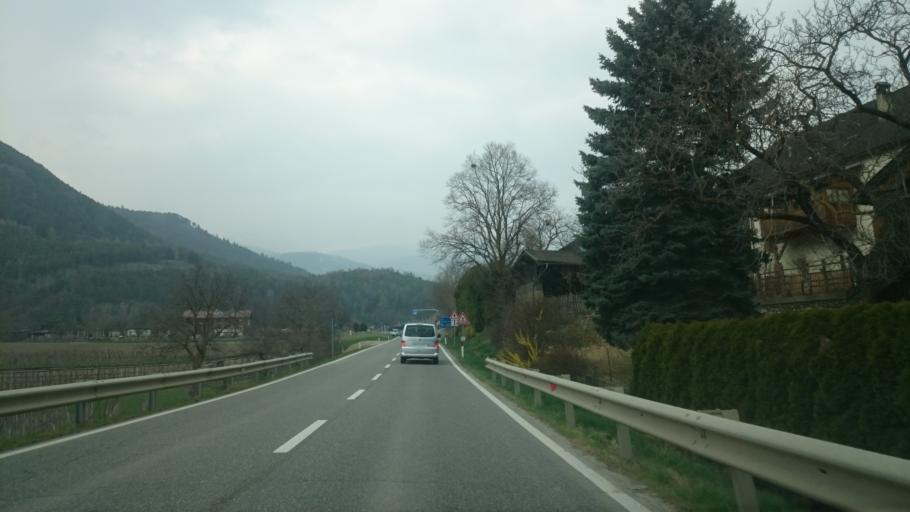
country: IT
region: Trentino-Alto Adige
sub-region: Bolzano
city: Naz-Sciaves - Natz-Schabs
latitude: 46.7702
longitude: 11.6647
